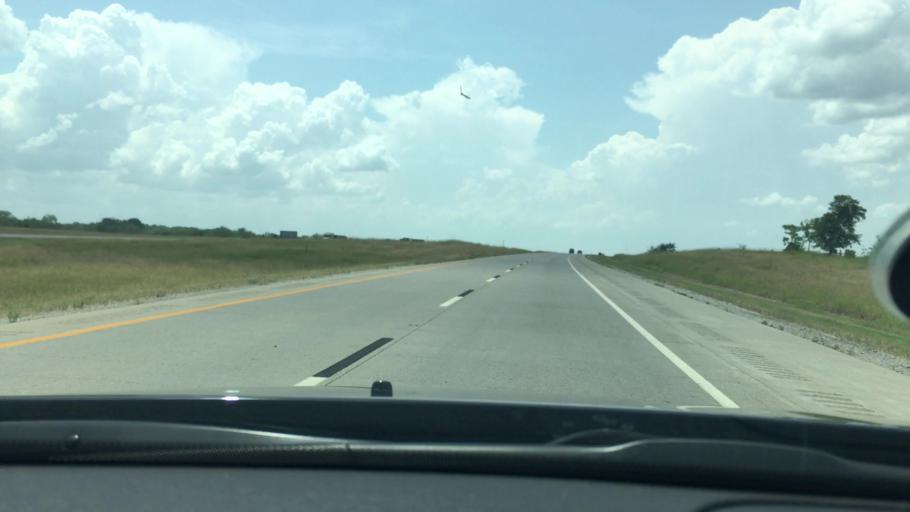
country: US
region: Oklahoma
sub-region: Carter County
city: Ardmore
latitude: 34.1055
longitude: -97.1519
